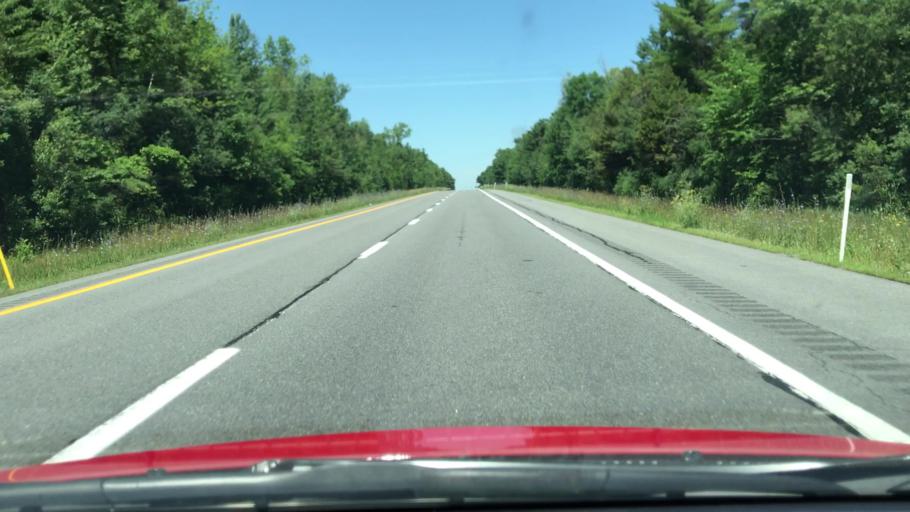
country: US
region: New York
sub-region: Clinton County
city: Champlain
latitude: 44.9561
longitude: -73.4488
